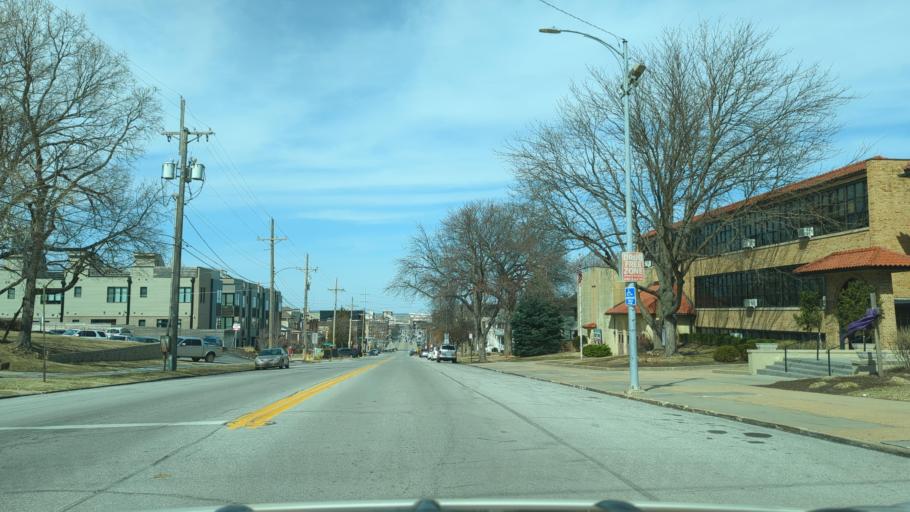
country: US
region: Nebraska
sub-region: Douglas County
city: Omaha
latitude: 41.2455
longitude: -95.9293
